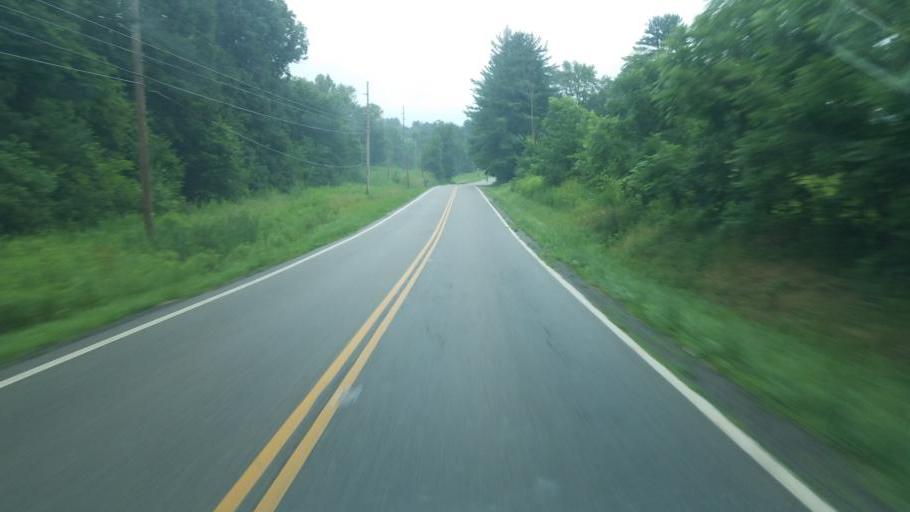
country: US
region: Ohio
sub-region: Tuscarawas County
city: Rockford
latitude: 40.4385
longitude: -81.2027
